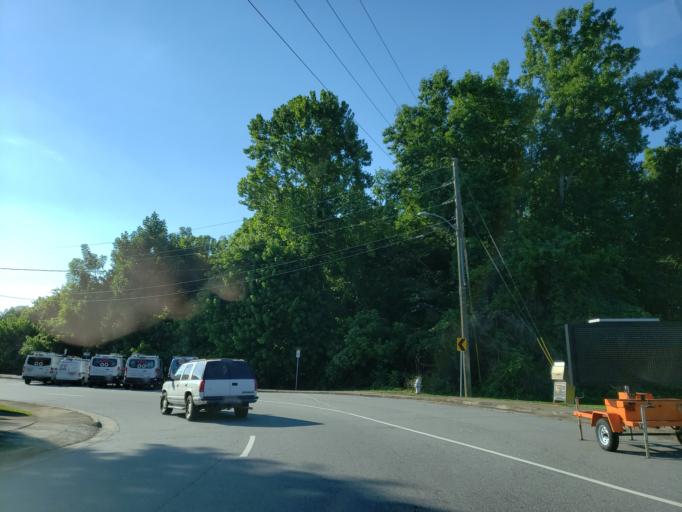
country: US
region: Georgia
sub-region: Cherokee County
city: Canton
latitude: 34.2369
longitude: -84.4877
